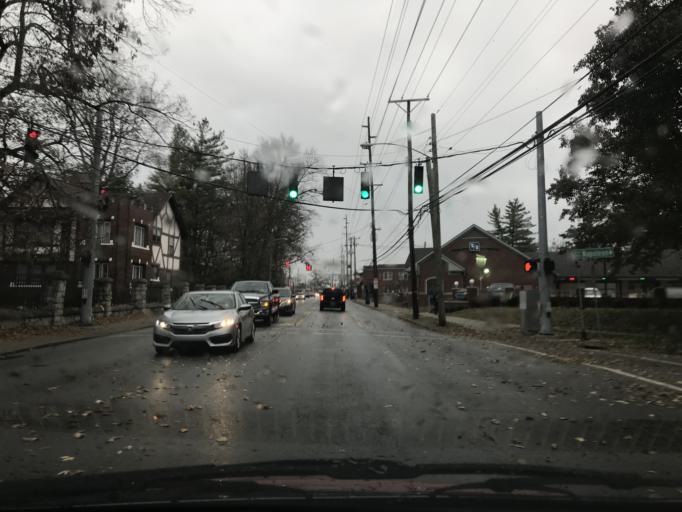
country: US
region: Kentucky
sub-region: Jefferson County
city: Audubon Park
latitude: 38.2257
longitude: -85.6966
